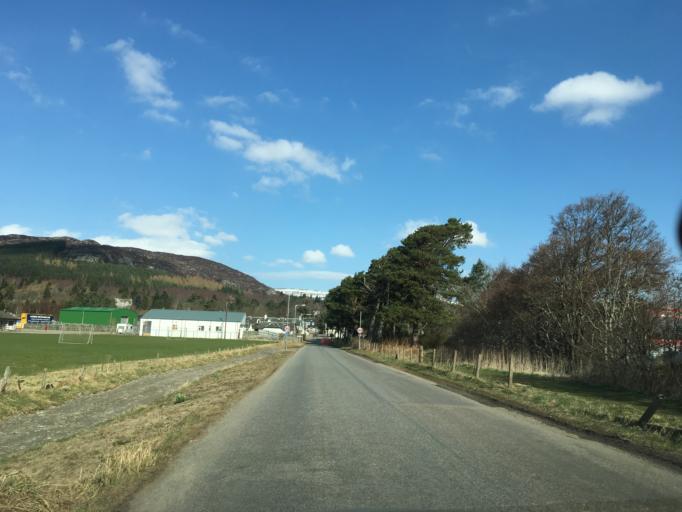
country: GB
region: Scotland
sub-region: Highland
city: Kingussie
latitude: 57.0757
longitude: -4.0502
